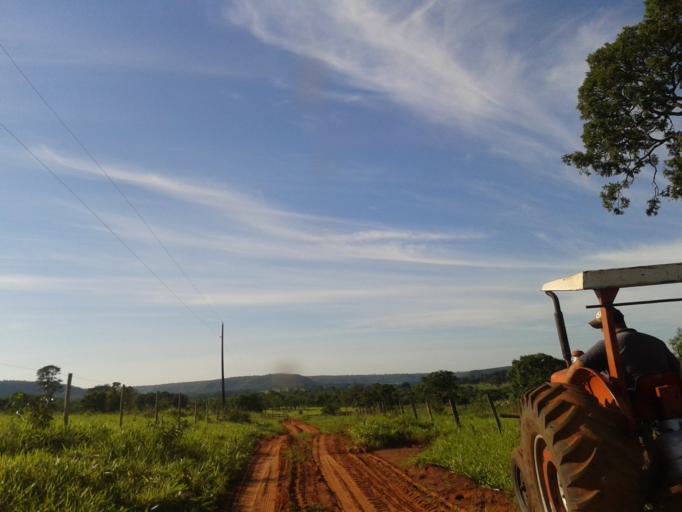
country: BR
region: Minas Gerais
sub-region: Santa Vitoria
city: Santa Vitoria
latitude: -19.0746
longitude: -49.9531
